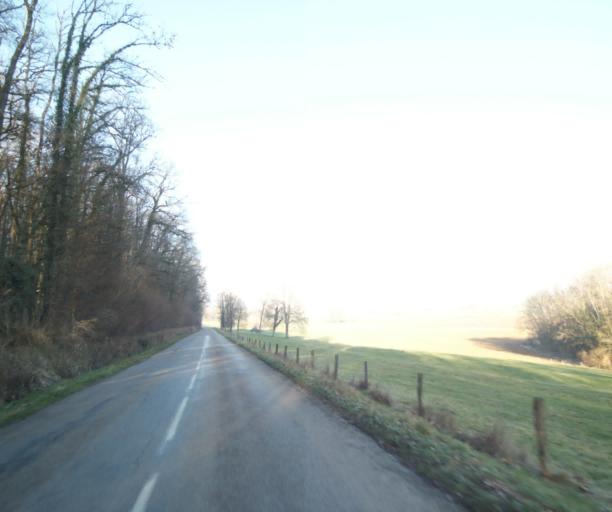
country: FR
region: Champagne-Ardenne
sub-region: Departement de la Haute-Marne
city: Bienville
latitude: 48.5744
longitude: 5.0803
